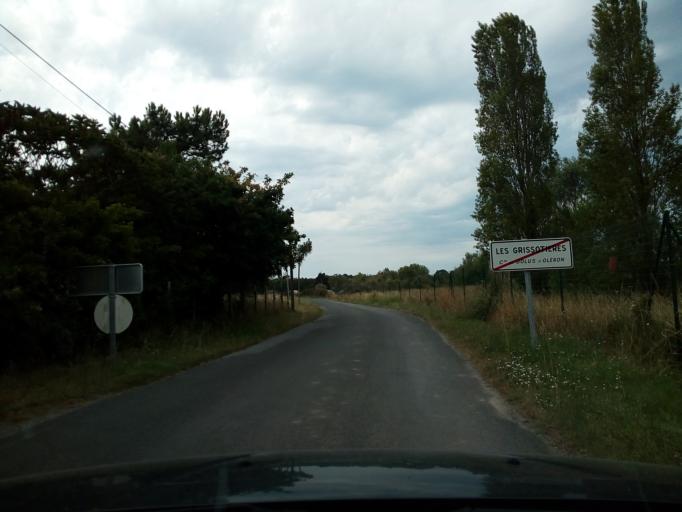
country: FR
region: Poitou-Charentes
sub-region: Departement de la Charente-Maritime
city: Dolus-d'Oleron
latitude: 45.9219
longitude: -1.2738
